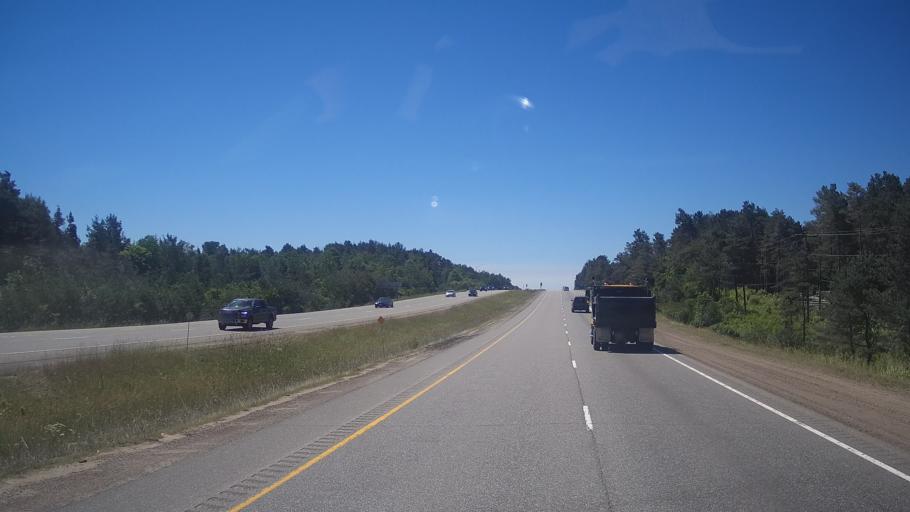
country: CA
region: Ontario
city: Bracebridge
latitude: 45.0758
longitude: -79.2969
